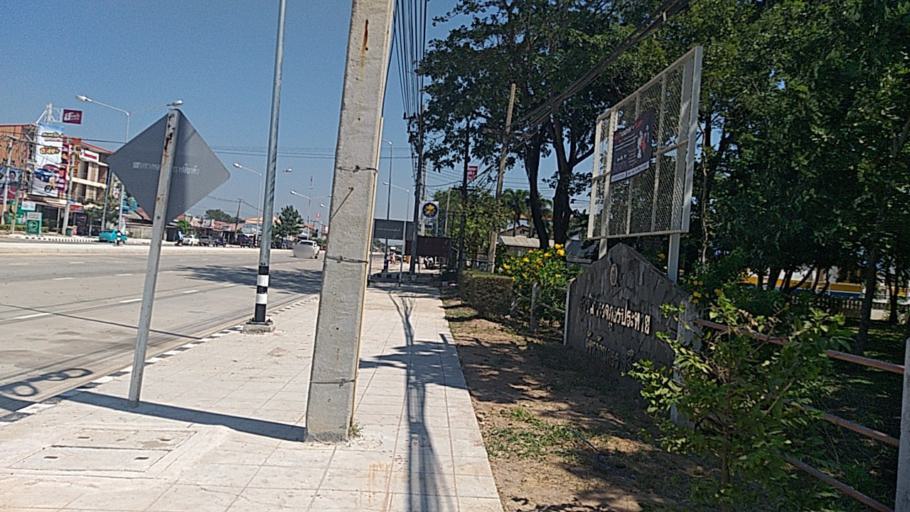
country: TH
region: Nakhon Ratchasima
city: Prathai
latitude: 15.5349
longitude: 102.7228
